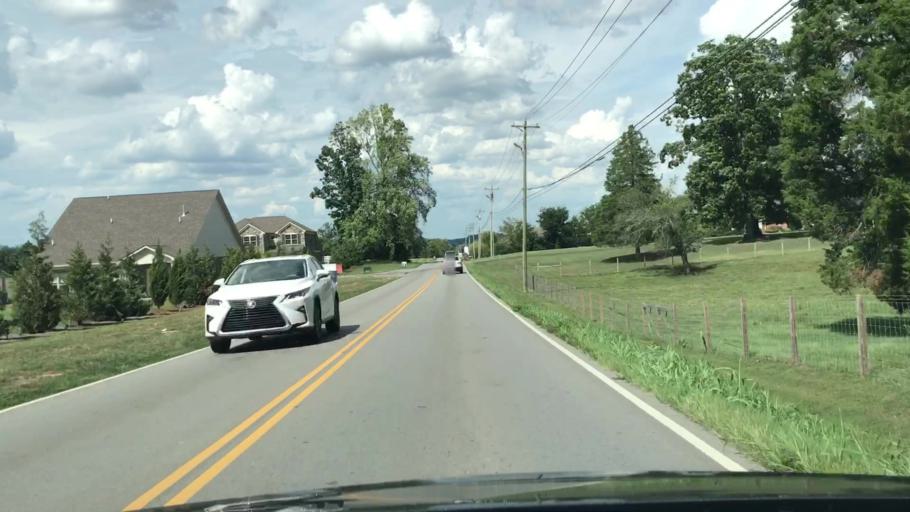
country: US
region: Tennessee
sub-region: Maury County
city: Spring Hill
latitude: 35.7564
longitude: -86.8831
